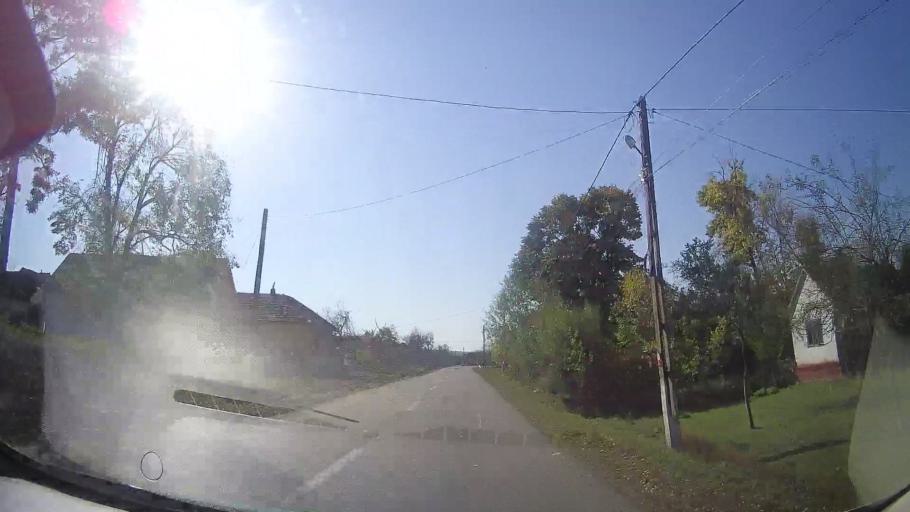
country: RO
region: Timis
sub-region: Comuna Secas
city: Secas
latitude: 45.8463
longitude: 21.7931
